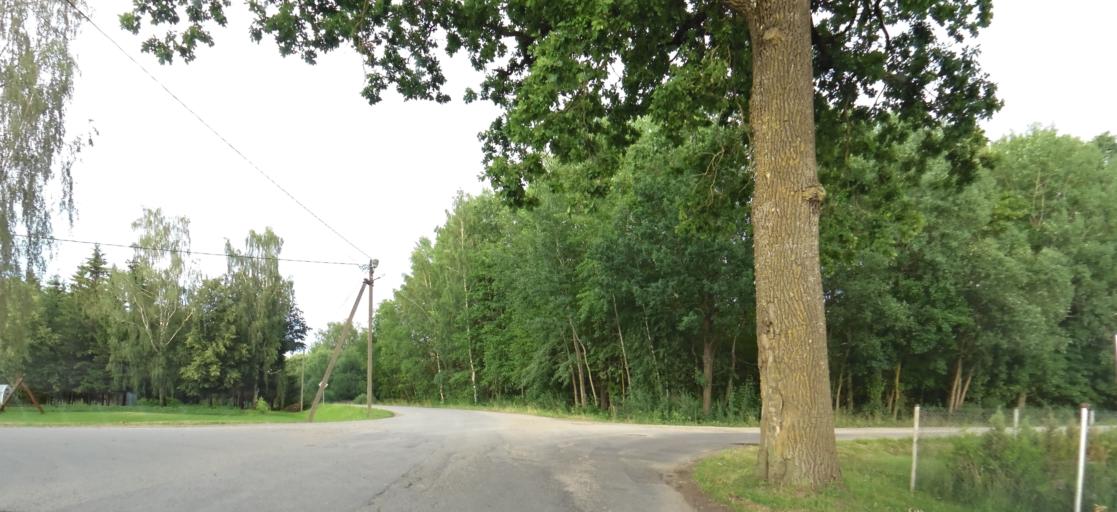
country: LT
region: Panevezys
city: Pasvalys
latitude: 56.0683
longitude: 24.4532
